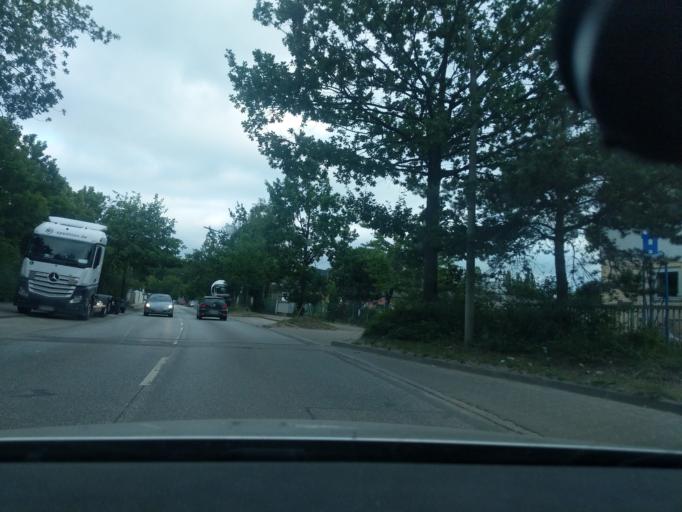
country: DE
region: Hamburg
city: Eidelstedt
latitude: 53.5891
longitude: 9.9073
